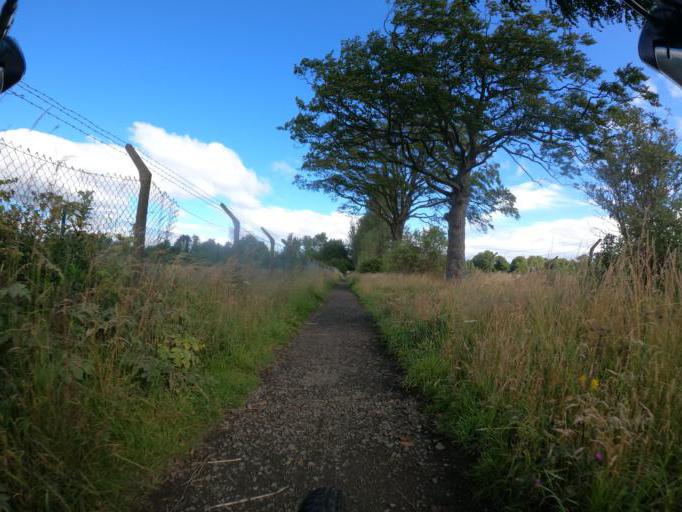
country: GB
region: Scotland
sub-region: Edinburgh
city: Edinburgh
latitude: 55.9763
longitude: -3.2607
